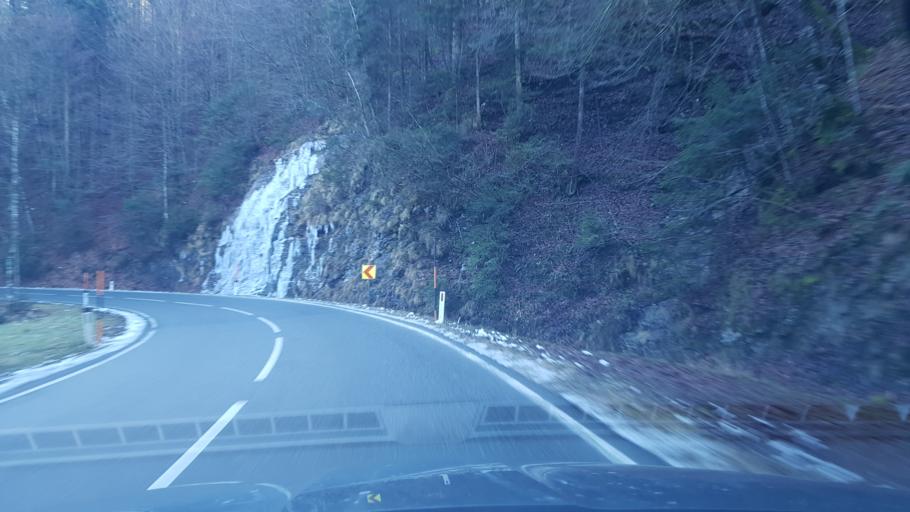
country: AT
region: Salzburg
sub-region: Politischer Bezirk Hallein
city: Krispl
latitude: 47.7285
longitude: 13.1701
